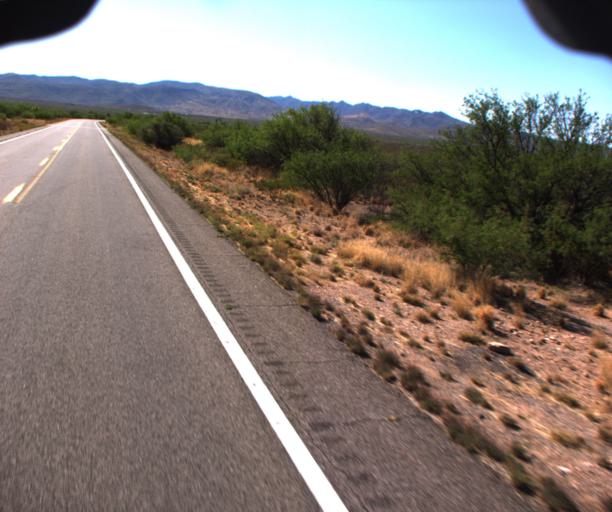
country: US
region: Arizona
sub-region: Cochise County
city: Tombstone
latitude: 31.5796
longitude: -110.0326
